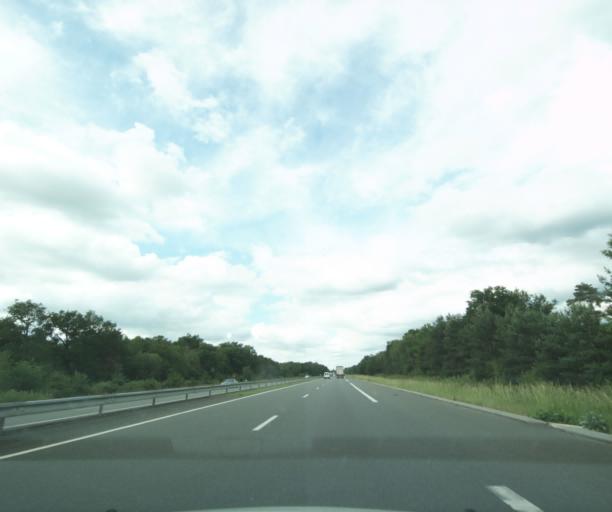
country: FR
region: Centre
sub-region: Departement du Loir-et-Cher
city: Salbris
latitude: 47.4634
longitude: 2.0058
